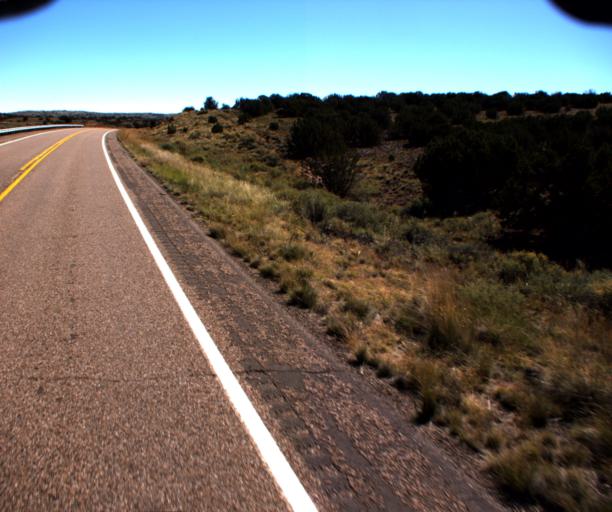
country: US
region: Arizona
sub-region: Apache County
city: Saint Johns
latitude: 34.5876
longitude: -109.5498
